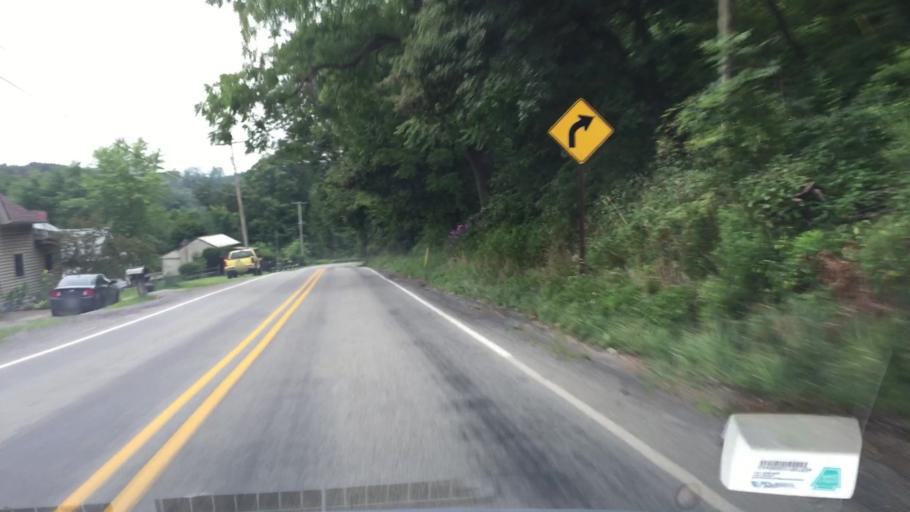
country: US
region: Pennsylvania
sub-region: Allegheny County
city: Curtisville
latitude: 40.6784
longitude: -79.8297
